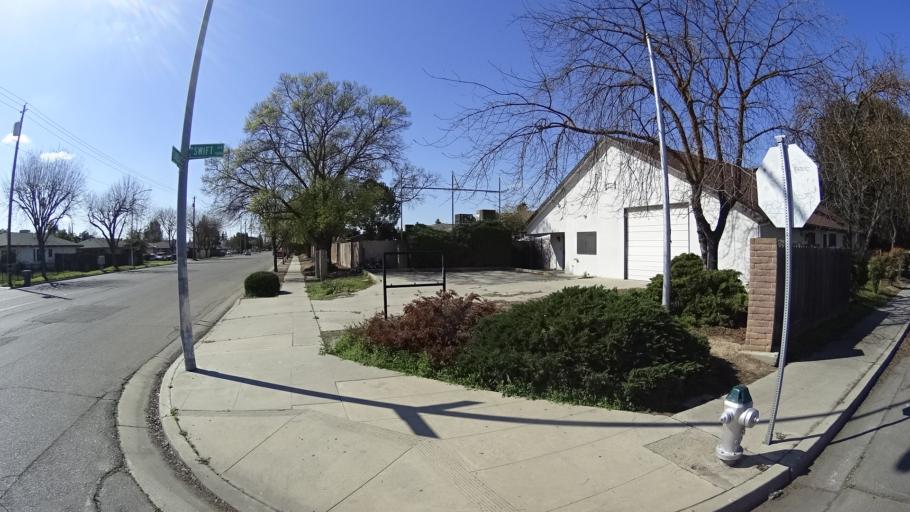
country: US
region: California
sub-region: Fresno County
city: West Park
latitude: 36.7963
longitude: -119.8806
